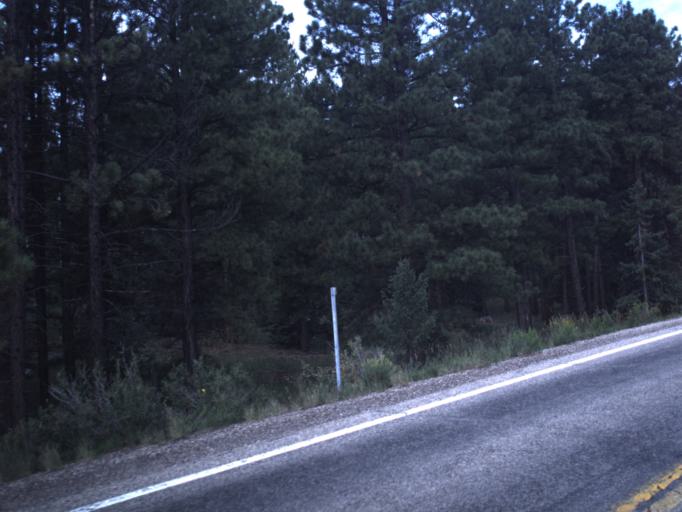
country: US
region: Utah
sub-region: Garfield County
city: Panguitch
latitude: 37.4924
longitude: -112.6185
